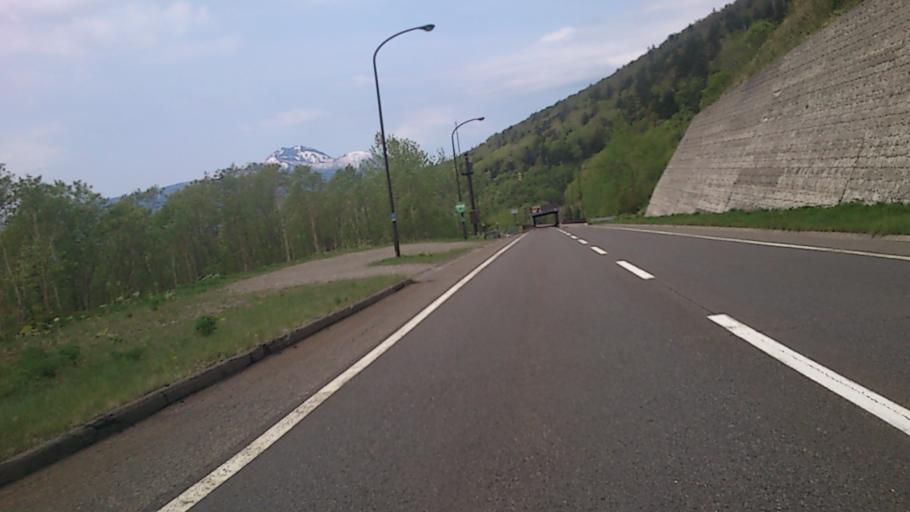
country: JP
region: Hokkaido
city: Kamikawa
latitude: 43.5723
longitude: 143.1220
